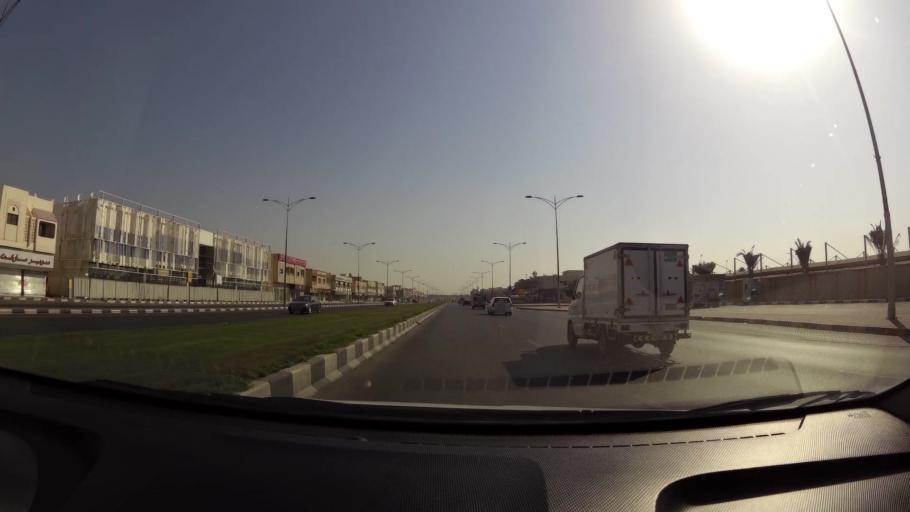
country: AE
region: Ash Shariqah
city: Sharjah
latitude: 25.3435
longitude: 55.4310
